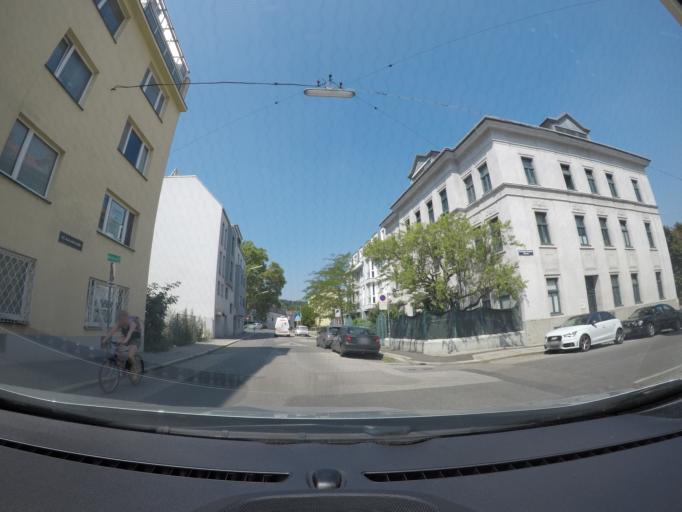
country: AT
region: Lower Austria
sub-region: Politischer Bezirk Modling
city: Perchtoldsdorf
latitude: 48.1949
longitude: 16.2618
